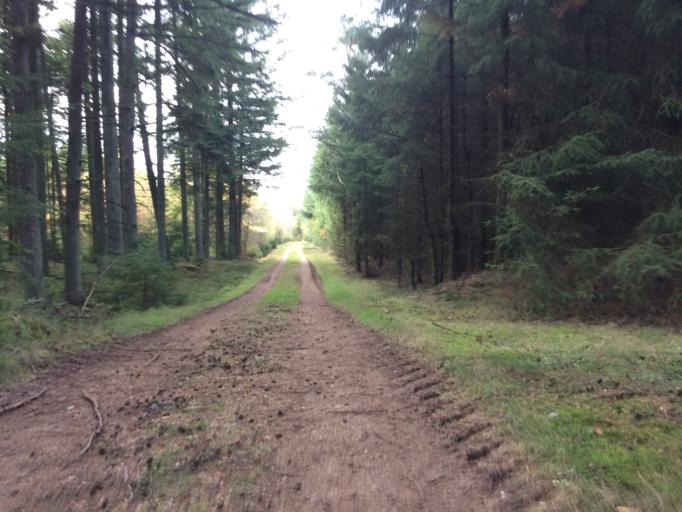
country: DK
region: Central Jutland
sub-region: Holstebro Kommune
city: Ulfborg
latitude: 56.2078
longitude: 8.4568
